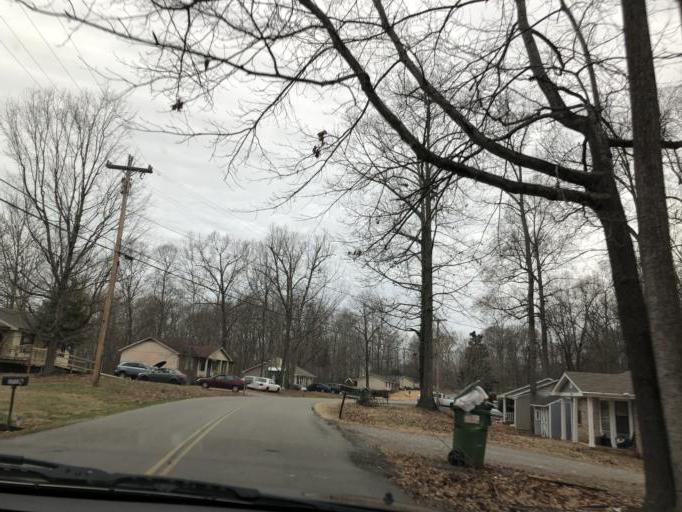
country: US
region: Tennessee
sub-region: Sumner County
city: White House
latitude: 36.4188
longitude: -86.6629
